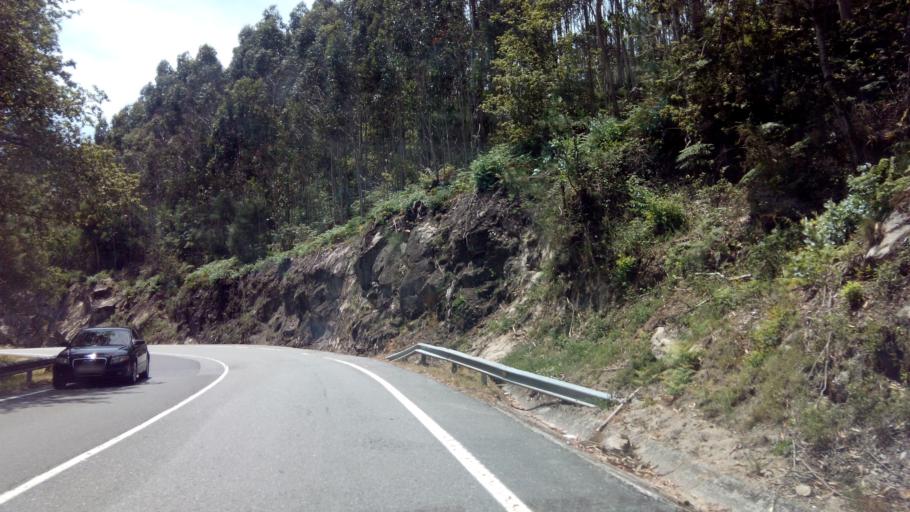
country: ES
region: Galicia
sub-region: Provincia de Pontevedra
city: Moana
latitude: 42.3277
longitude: -8.7203
